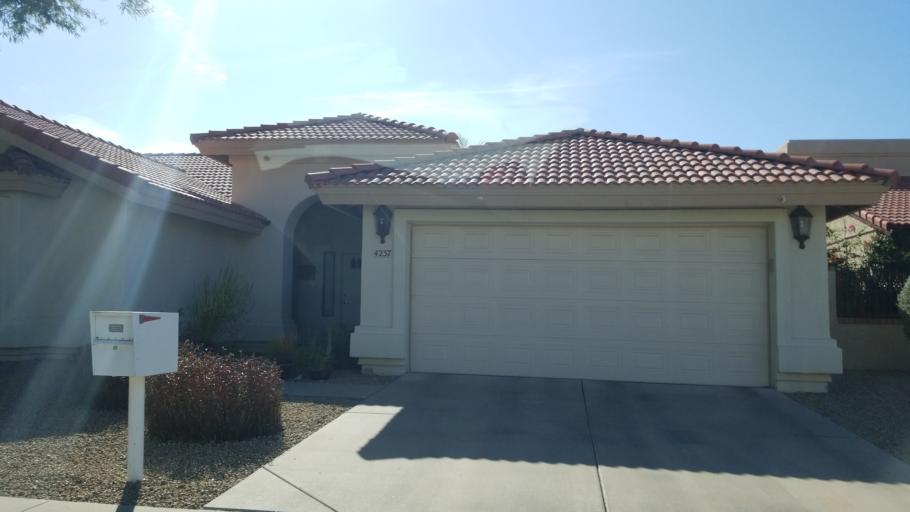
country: US
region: Arizona
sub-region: Maricopa County
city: Paradise Valley
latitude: 33.5921
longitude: -111.9888
